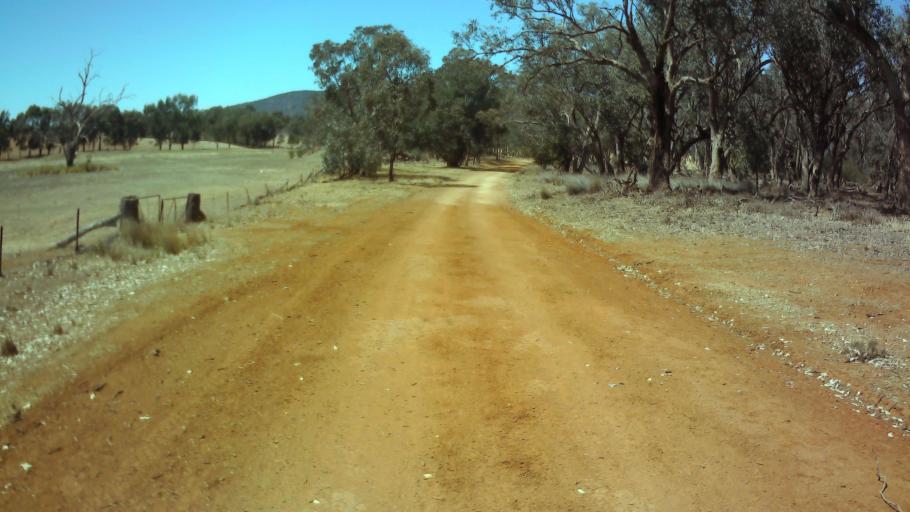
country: AU
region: New South Wales
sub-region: Weddin
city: Grenfell
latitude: -33.9526
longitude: 148.0847
